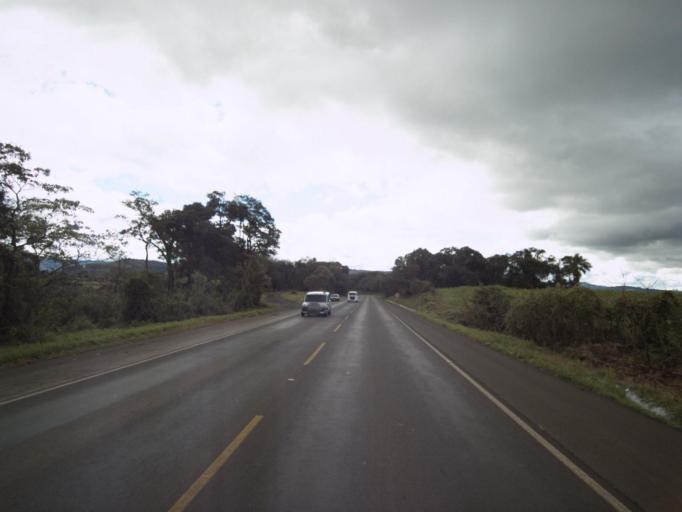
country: BR
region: Santa Catarina
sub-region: Concordia
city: Concordia
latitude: -27.1005
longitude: -51.9001
